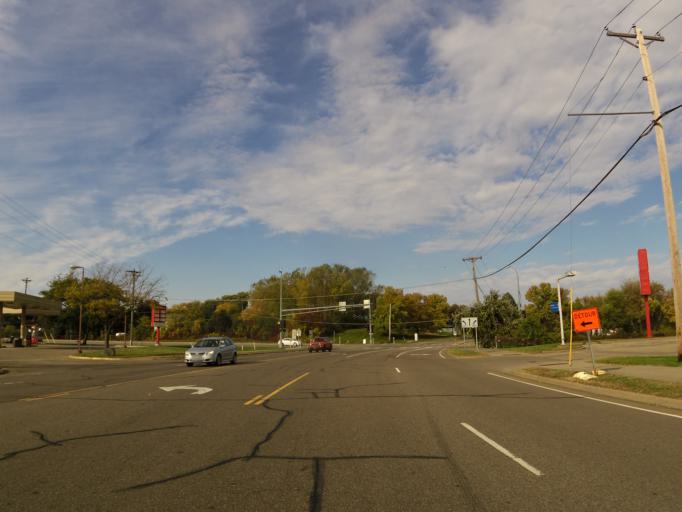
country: US
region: Minnesota
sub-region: Dakota County
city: Eagan
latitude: 44.8049
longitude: -93.2275
